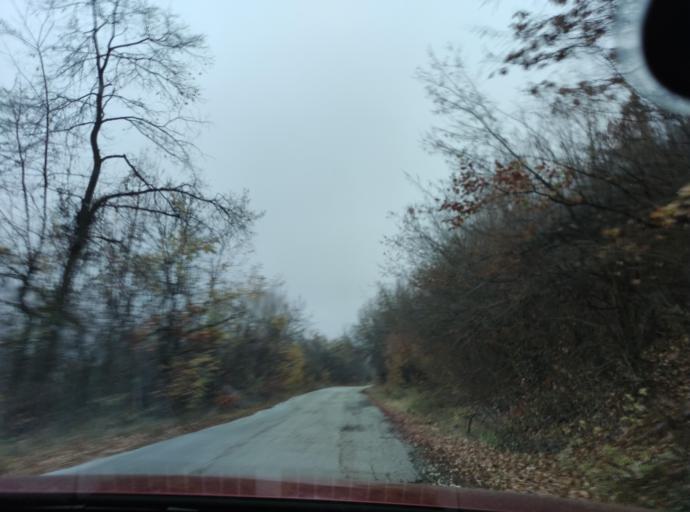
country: BG
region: Lovech
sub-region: Obshtina Yablanitsa
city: Yablanitsa
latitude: 43.1015
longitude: 24.0717
